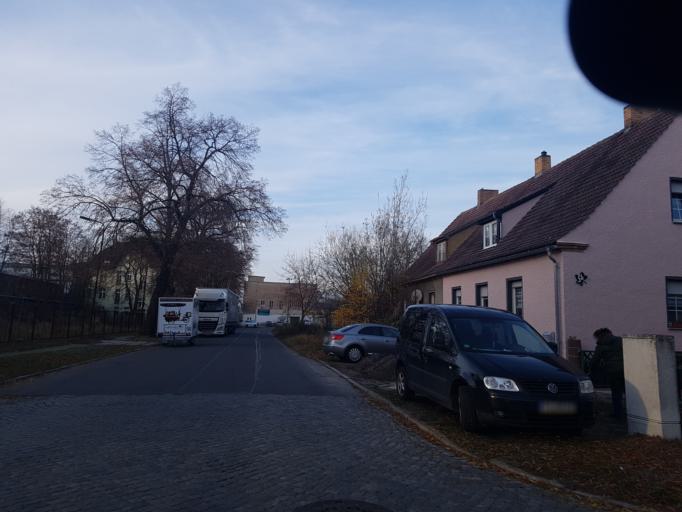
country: DE
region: Brandenburg
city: Finsterwalde
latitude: 51.6371
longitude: 13.7195
